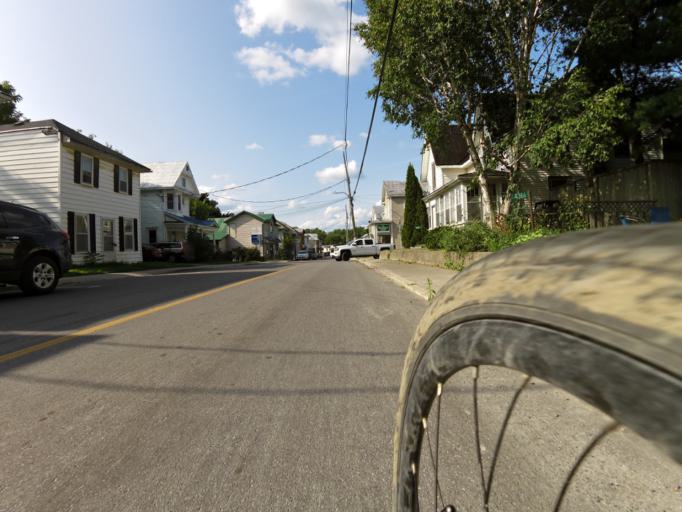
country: CA
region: Ontario
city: Kingston
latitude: 44.4093
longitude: -76.5966
